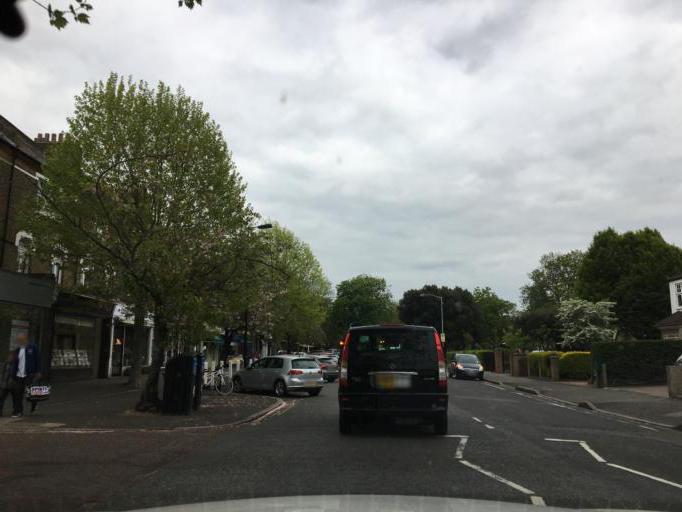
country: GB
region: England
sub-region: Greater London
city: Camberwell
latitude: 51.4515
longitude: -0.0863
